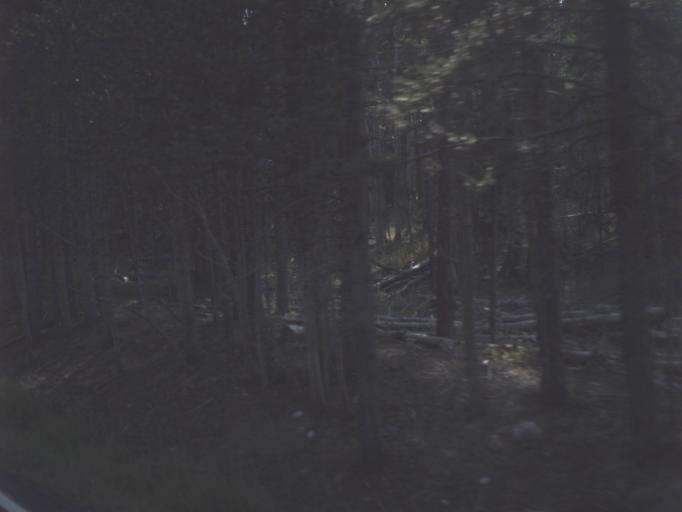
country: US
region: Utah
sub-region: Summit County
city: Oakley
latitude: 40.8141
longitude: -110.8725
